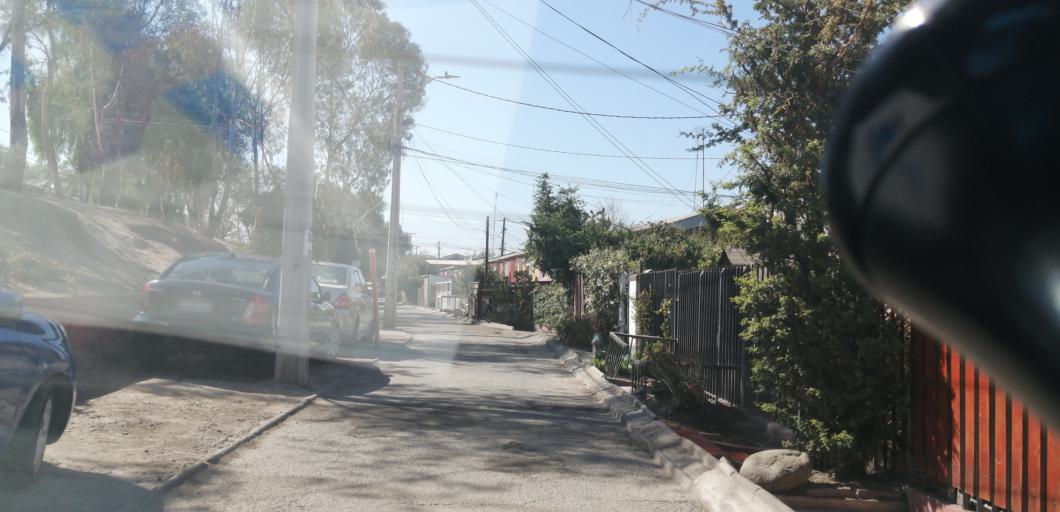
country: CL
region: Santiago Metropolitan
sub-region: Provincia de Santiago
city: Lo Prado
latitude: -33.4466
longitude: -70.7567
